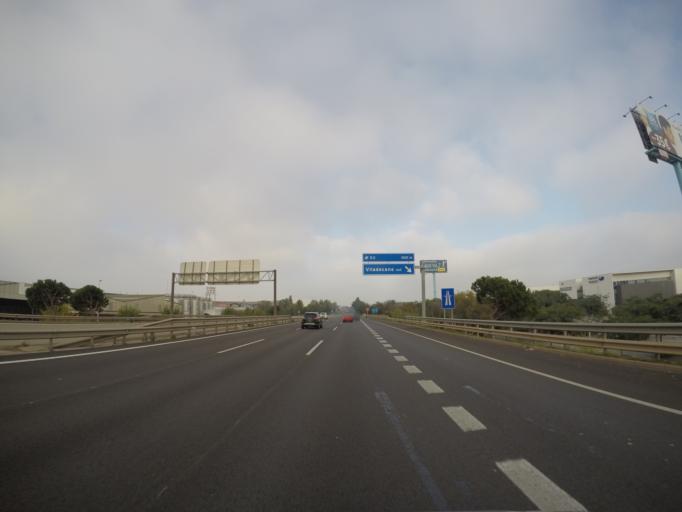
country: ES
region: Catalonia
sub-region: Provincia de Barcelona
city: Gava
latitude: 41.2948
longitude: 2.0138
